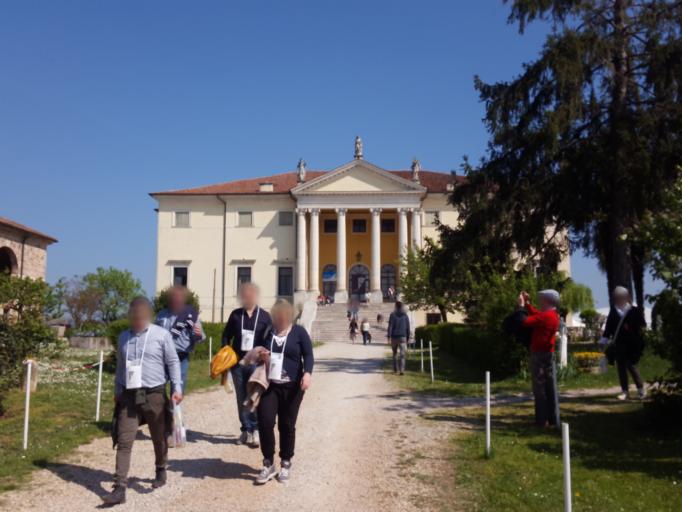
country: IT
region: Veneto
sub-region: Provincia di Vicenza
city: Monticello di Fara
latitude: 45.4318
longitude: 11.3949
